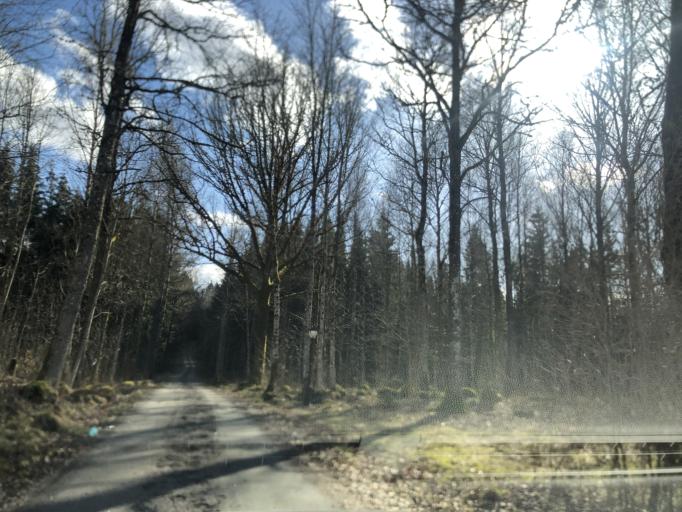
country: SE
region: Vaestra Goetaland
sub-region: Ulricehamns Kommun
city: Ulricehamn
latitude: 57.6919
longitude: 13.3756
